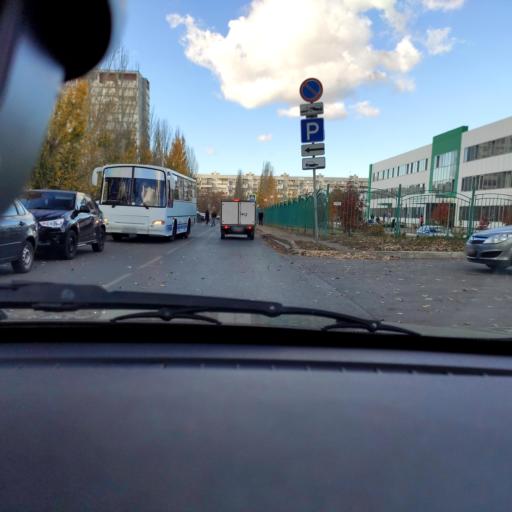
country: RU
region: Samara
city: Tol'yatti
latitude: 53.5370
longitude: 49.3375
